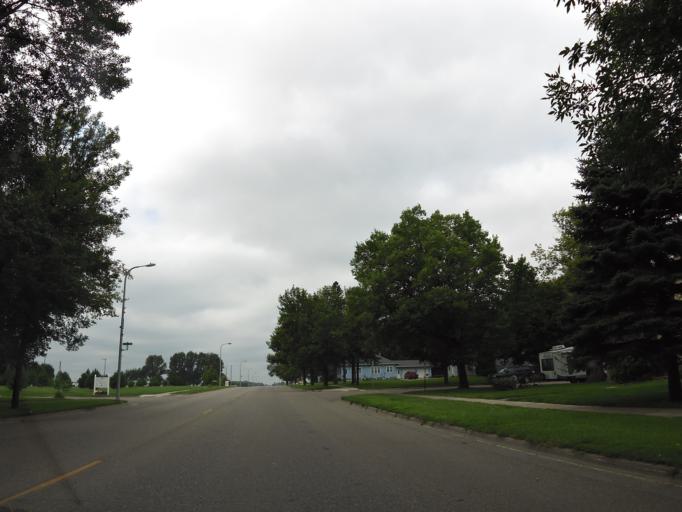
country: US
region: Minnesota
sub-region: Renville County
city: Renville
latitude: 44.7892
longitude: -95.2145
